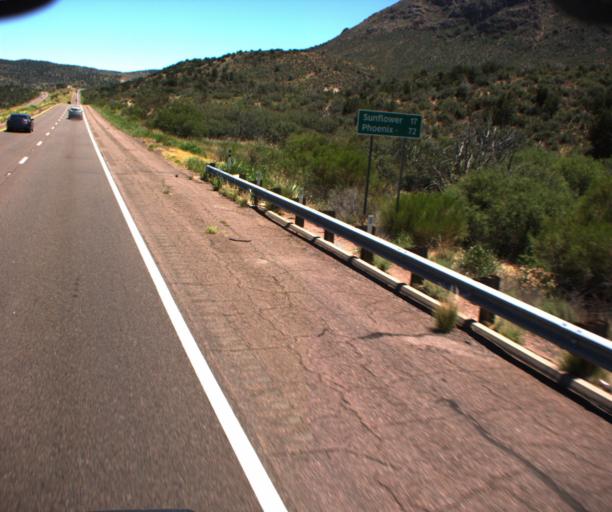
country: US
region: Arizona
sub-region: Gila County
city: Payson
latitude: 34.0344
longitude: -111.3671
